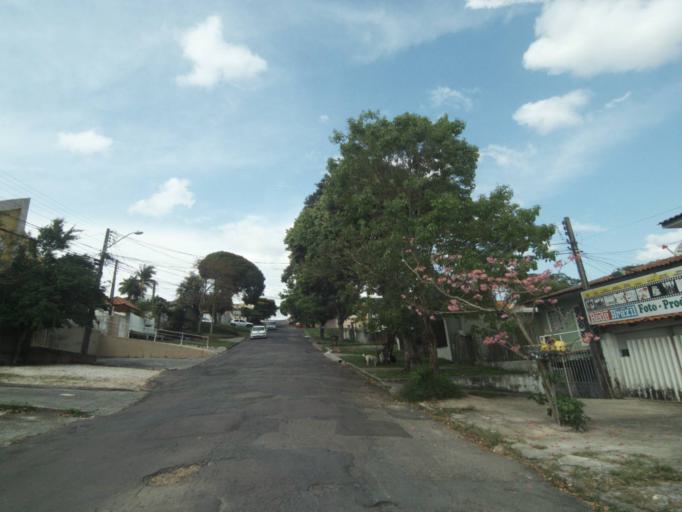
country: BR
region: Parana
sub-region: Pinhais
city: Pinhais
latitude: -25.4019
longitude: -49.2030
